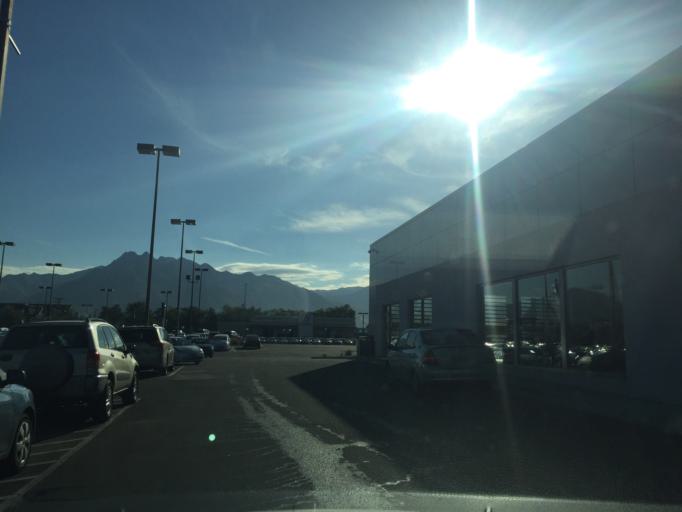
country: US
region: Utah
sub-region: Salt Lake County
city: Murray
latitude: 40.6489
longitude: -111.8899
